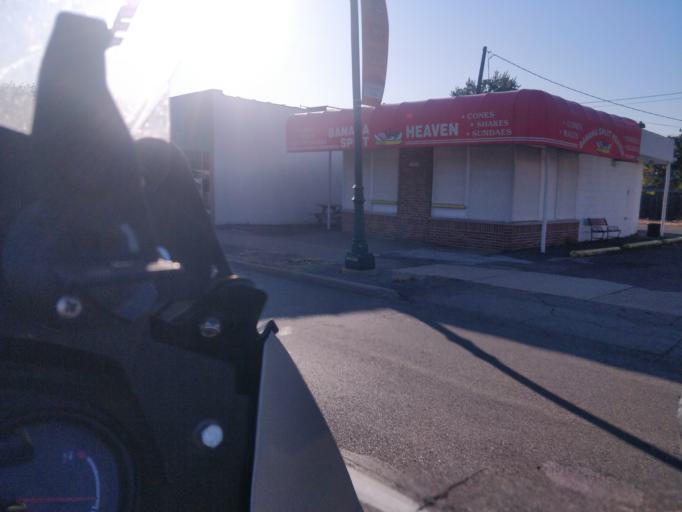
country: US
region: Michigan
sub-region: Wayne County
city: Melvindale
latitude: 42.2790
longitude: -83.1900
